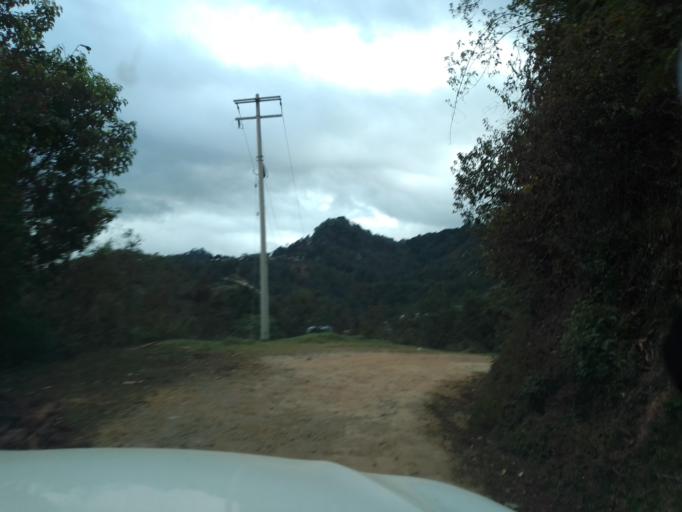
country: MX
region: Chiapas
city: Motozintla de Mendoza
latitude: 15.2155
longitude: -92.2287
